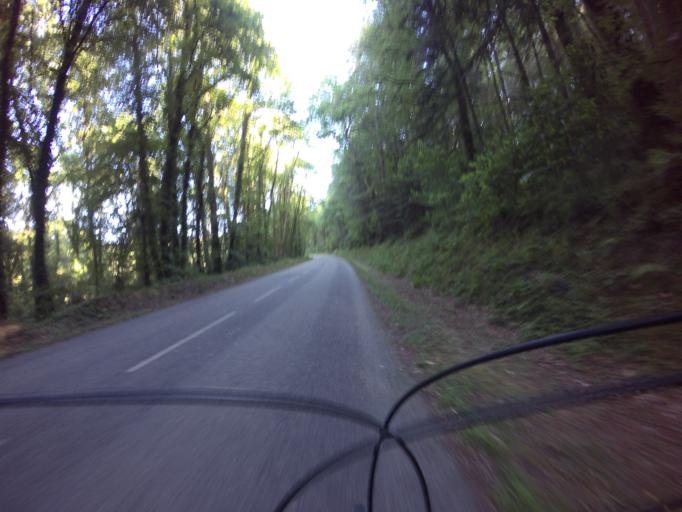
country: FR
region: Brittany
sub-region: Departement du Finistere
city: Quimper
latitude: 48.0221
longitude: -4.1382
